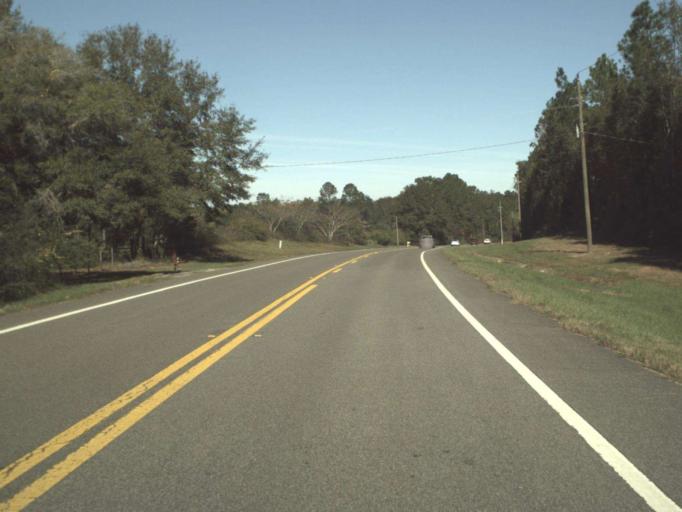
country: US
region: Florida
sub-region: Okaloosa County
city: Crestview
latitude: 30.8583
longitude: -86.6742
